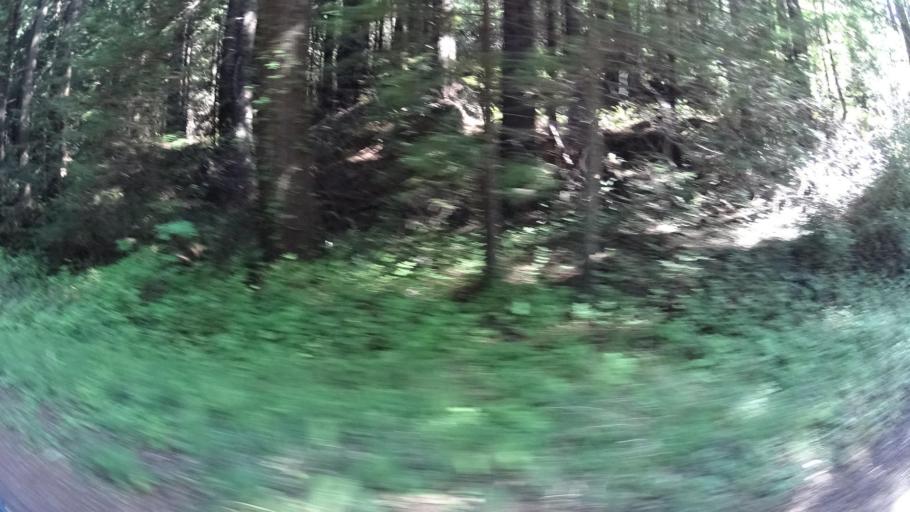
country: US
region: California
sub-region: Humboldt County
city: Rio Dell
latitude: 40.4586
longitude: -124.0145
